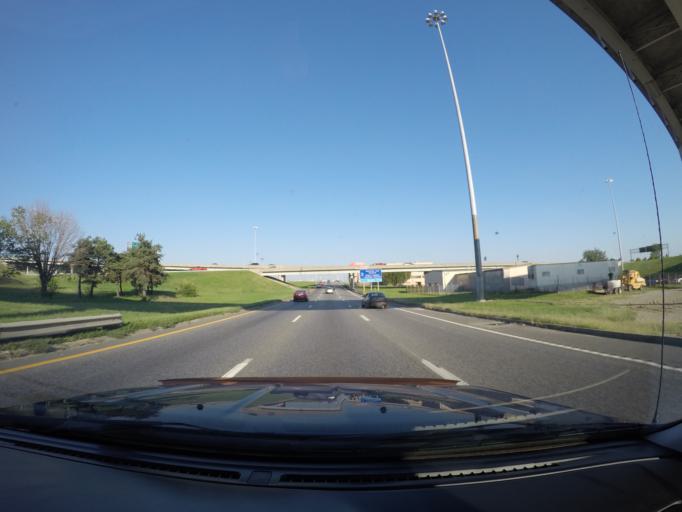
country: US
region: Missouri
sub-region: Jackson County
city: Kansas City
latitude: 39.0962
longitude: -94.5728
